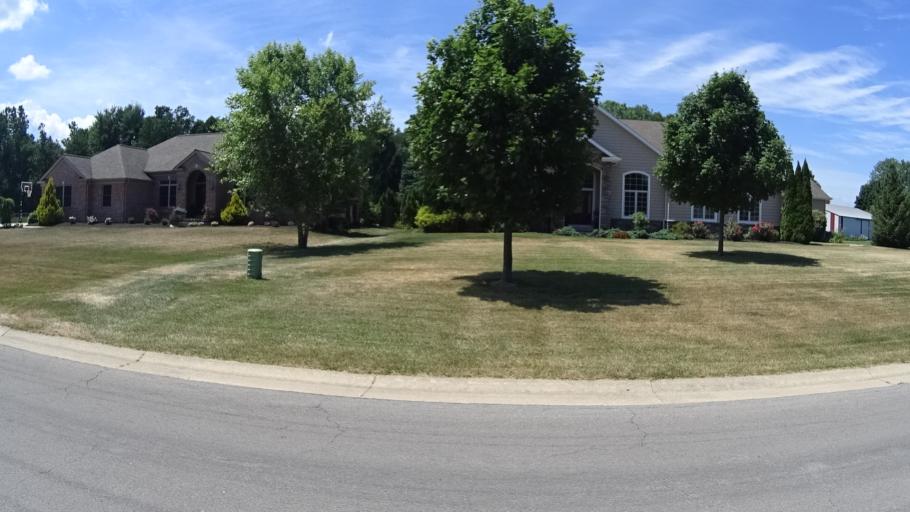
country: US
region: Ohio
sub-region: Erie County
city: Sandusky
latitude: 41.3948
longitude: -82.6758
